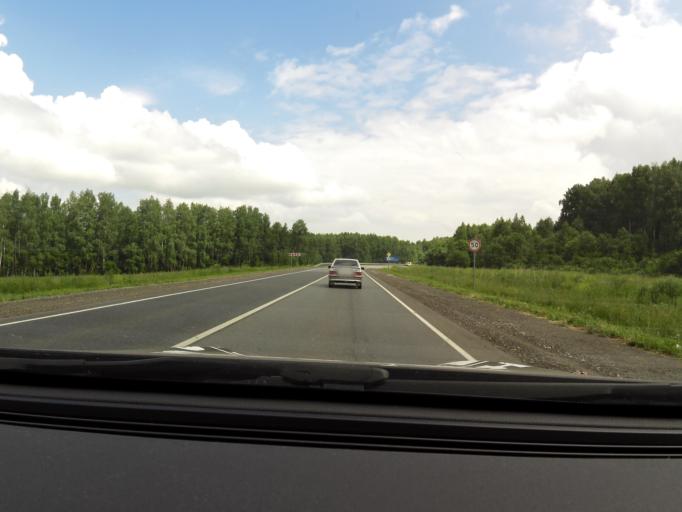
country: RU
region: Perm
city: Suksun
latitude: 57.1616
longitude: 57.2429
